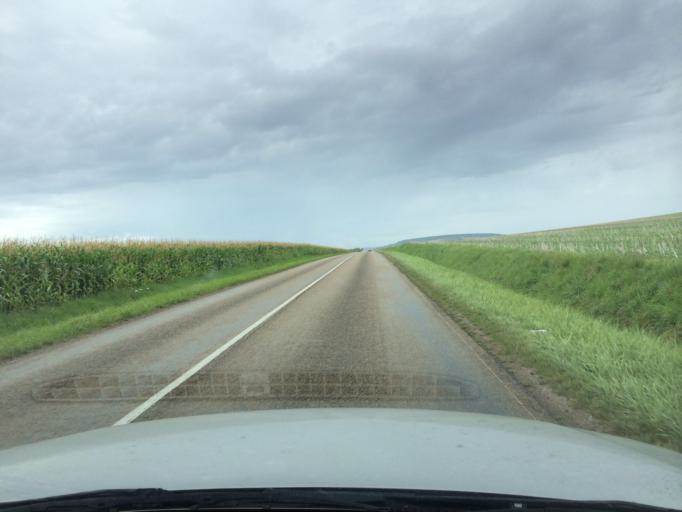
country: FR
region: Bourgogne
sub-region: Departement de l'Yonne
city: Aillant-sur-Tholon
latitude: 47.8815
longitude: 3.3517
